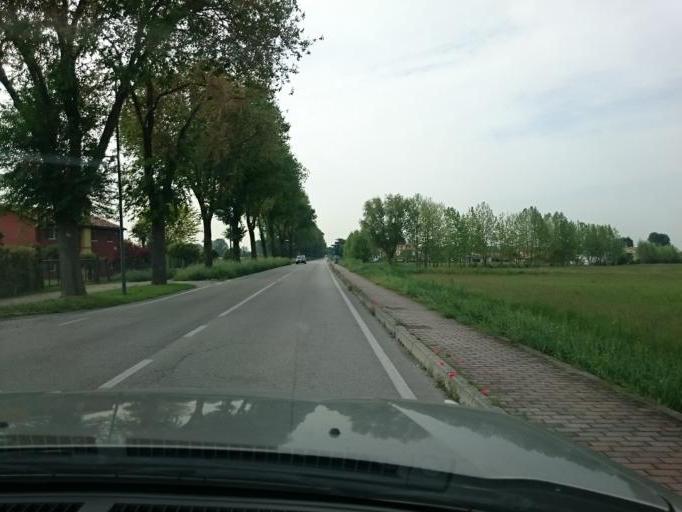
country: IT
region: Veneto
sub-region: Provincia di Venezia
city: Fornase
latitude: 45.4429
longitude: 12.1968
